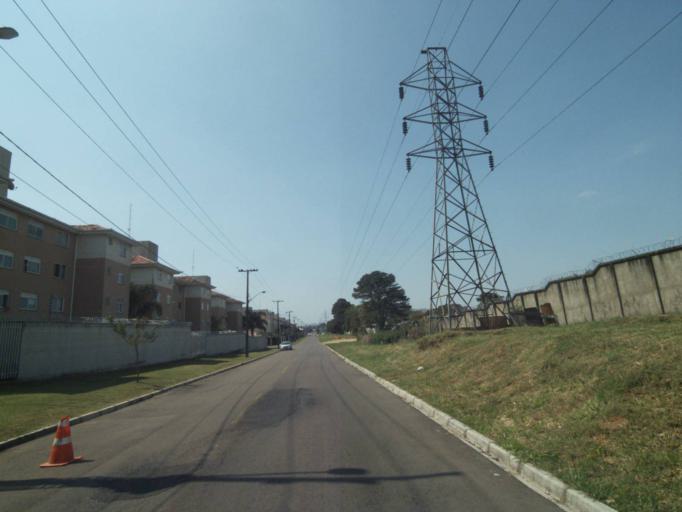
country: BR
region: Parana
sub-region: Curitiba
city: Curitiba
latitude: -25.4875
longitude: -49.3230
